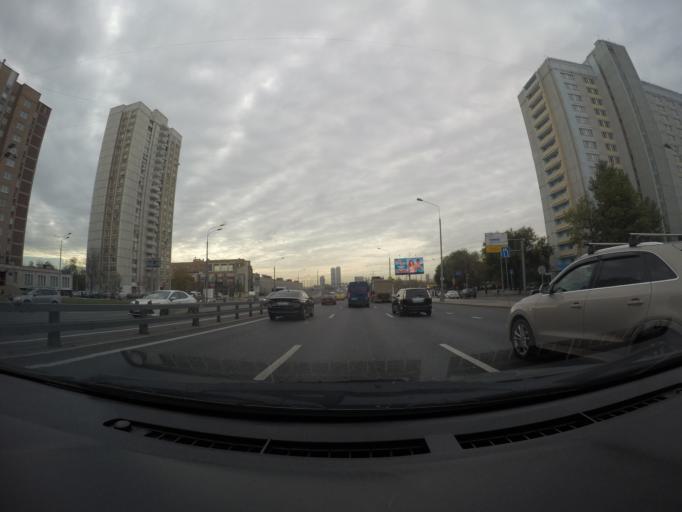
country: RU
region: Moscow
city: Rostokino
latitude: 55.8528
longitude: 37.6794
